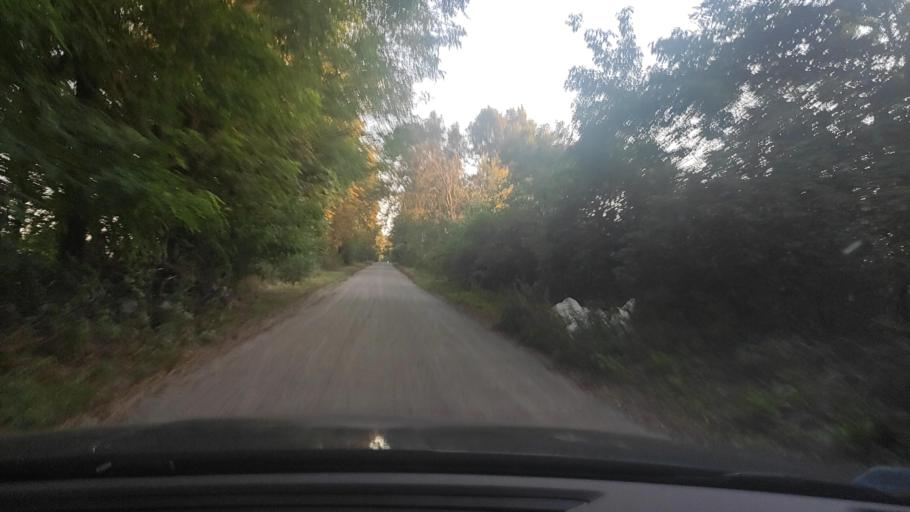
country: PL
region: Greater Poland Voivodeship
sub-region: Powiat poznanski
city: Swarzedz
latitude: 52.4394
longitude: 17.1231
